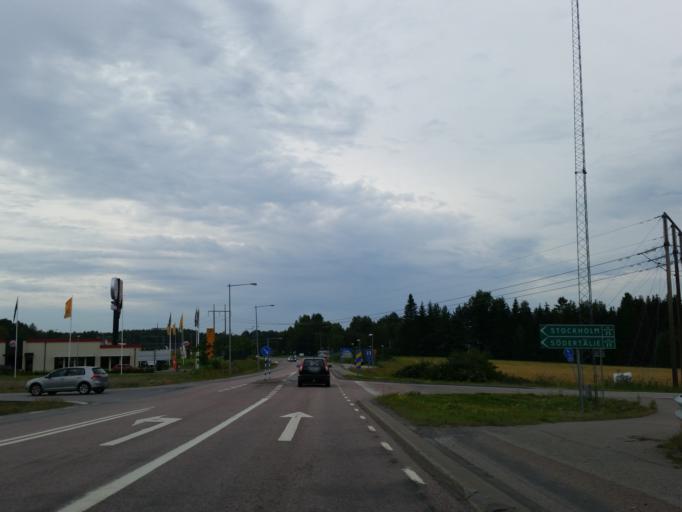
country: SE
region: Stockholm
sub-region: Nykvarns Kommun
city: Nykvarn
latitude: 59.1897
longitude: 17.4588
